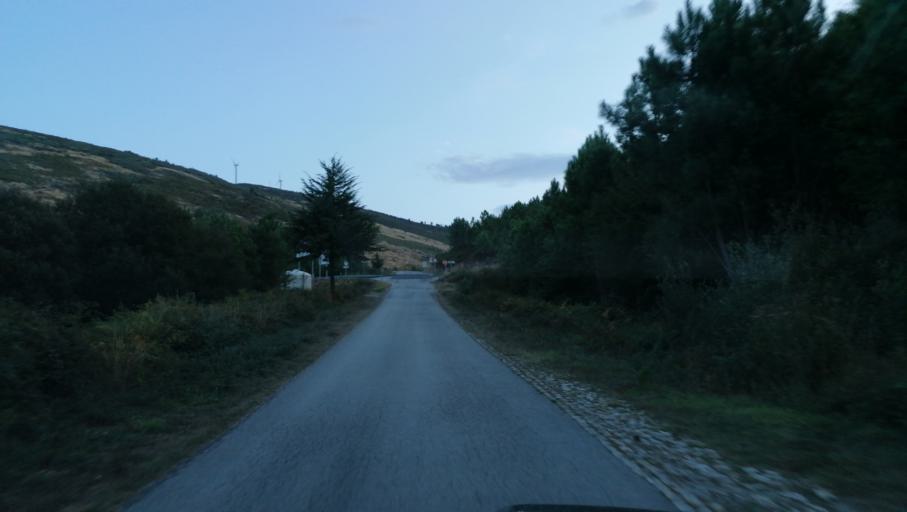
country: PT
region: Vila Real
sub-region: Vila Pouca de Aguiar
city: Vila Pouca de Aguiar
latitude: 41.5564
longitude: -7.7109
